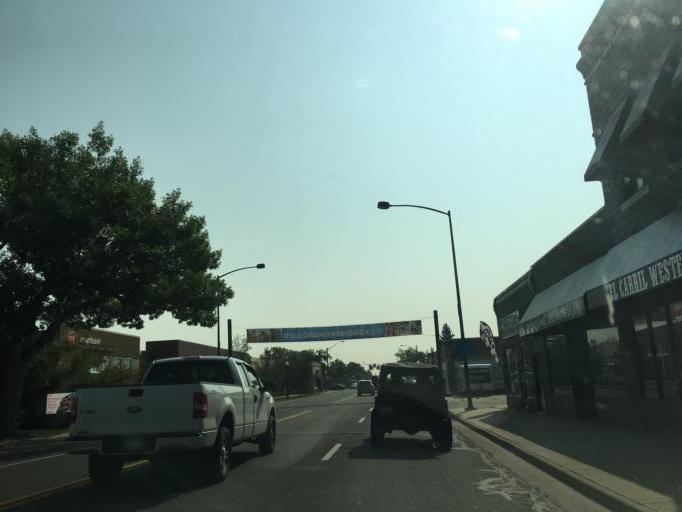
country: US
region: Colorado
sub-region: Adams County
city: Brighton
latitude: 39.9868
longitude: -104.8202
